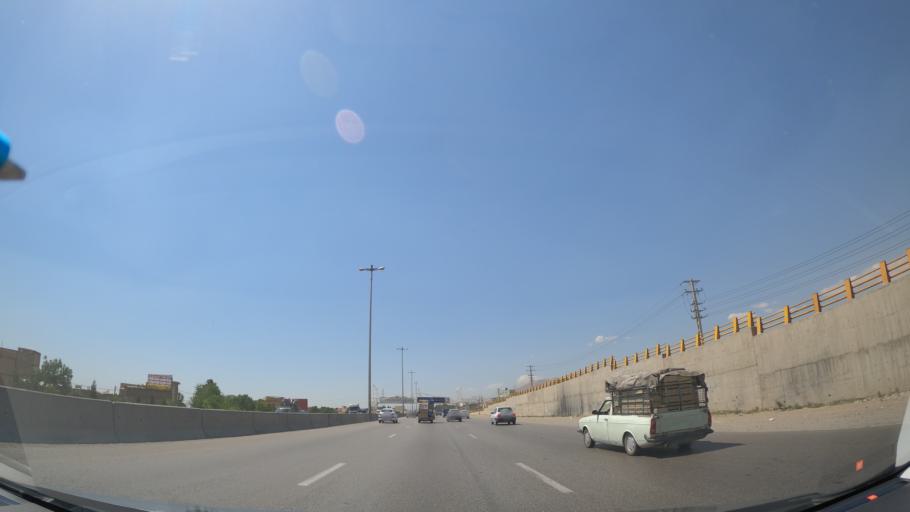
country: IR
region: Alborz
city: Karaj
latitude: 35.8658
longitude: 50.9024
